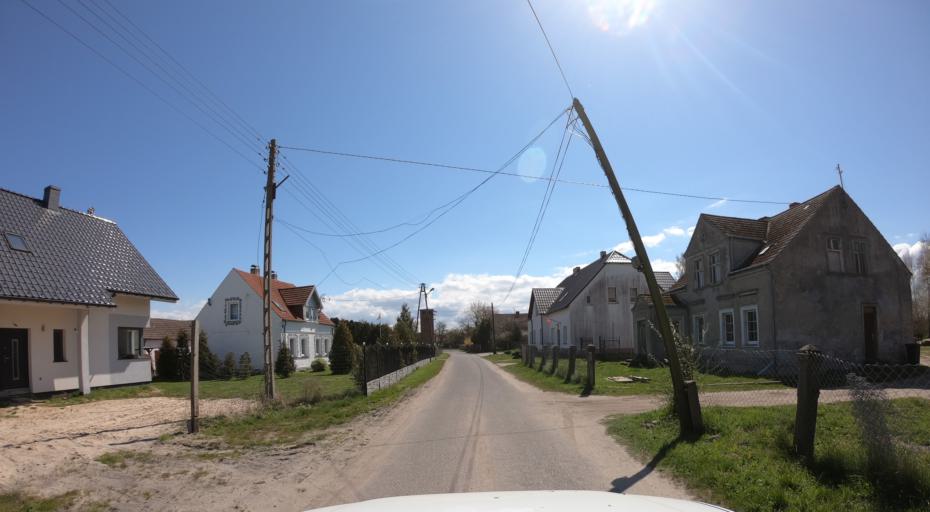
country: PL
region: West Pomeranian Voivodeship
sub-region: Powiat kamienski
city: Kamien Pomorski
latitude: 53.9494
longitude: 14.6845
